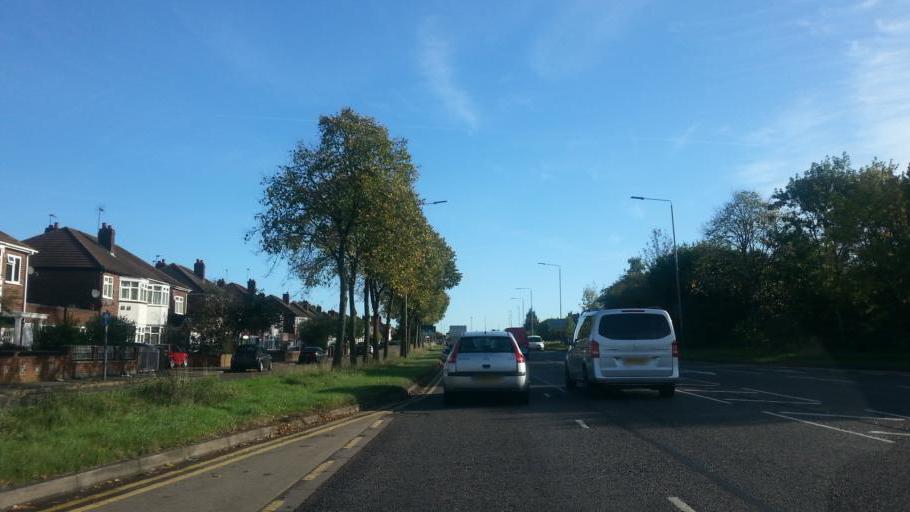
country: GB
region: England
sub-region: Leicestershire
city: Wigston Magna
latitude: 52.5989
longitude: -1.1191
